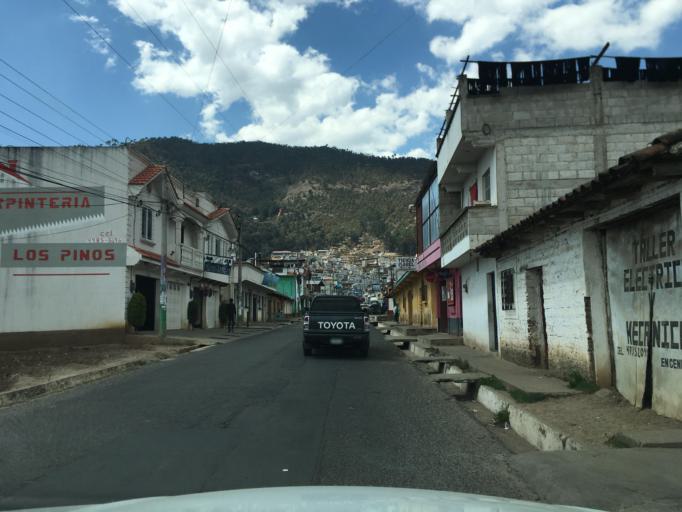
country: GT
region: Totonicapan
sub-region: Municipio de San Andres Xecul
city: San Andres Xecul
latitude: 14.9050
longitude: -91.4783
